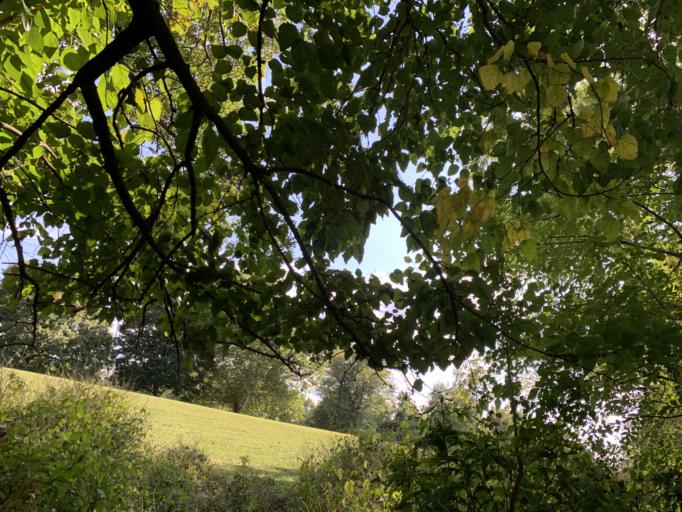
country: US
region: Indiana
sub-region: Floyd County
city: New Albany
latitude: 38.2723
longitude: -85.8255
